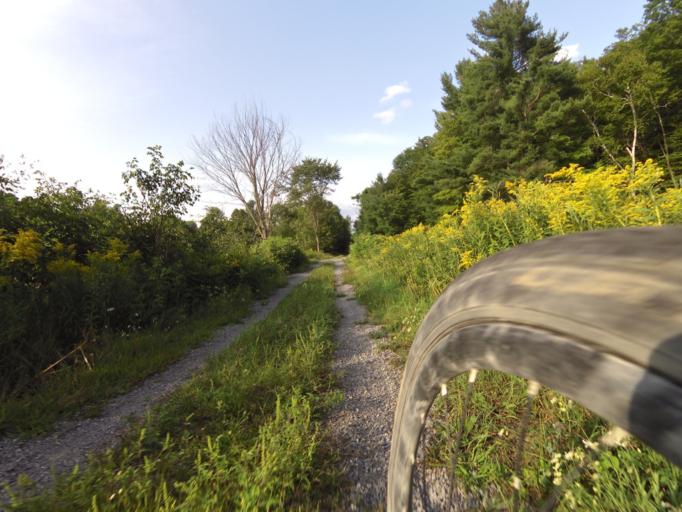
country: CA
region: Ontario
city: Kingston
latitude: 44.4931
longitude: -76.4516
